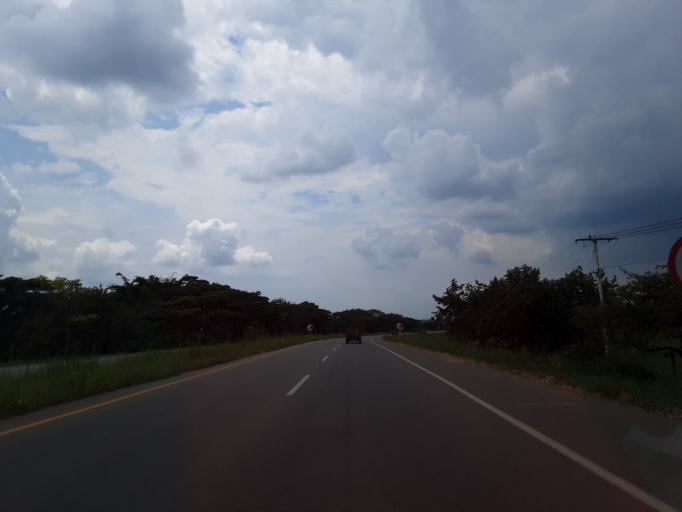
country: CO
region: Cauca
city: Santander de Quilichao
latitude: 3.0271
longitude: -76.4815
